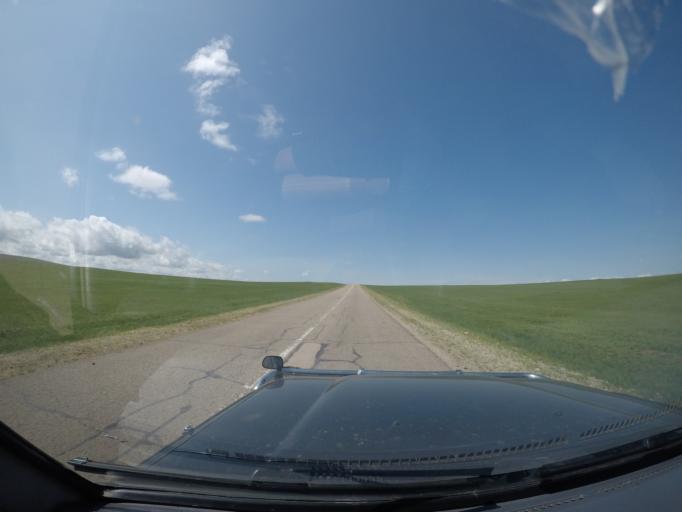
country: MN
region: Hentiy
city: Bayan
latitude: 47.2833
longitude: 110.9658
